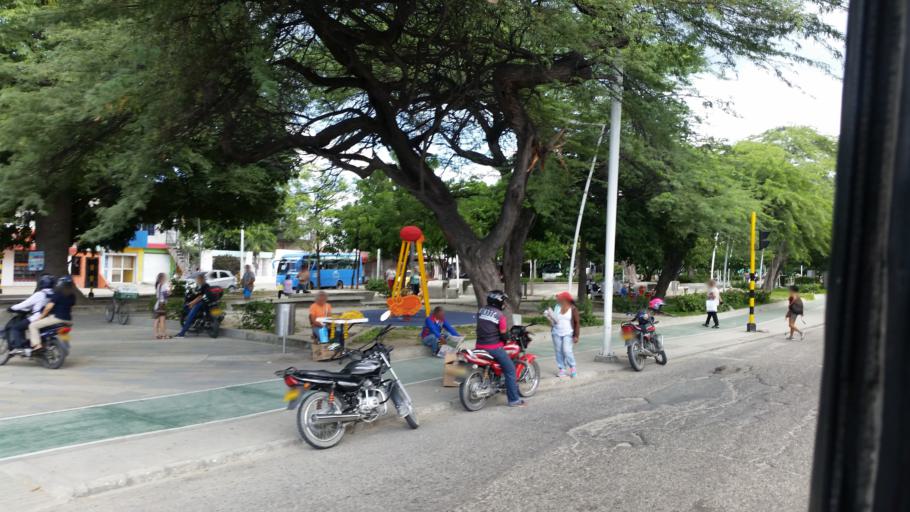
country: CO
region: Magdalena
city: Santa Marta
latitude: 11.2286
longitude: -74.1733
